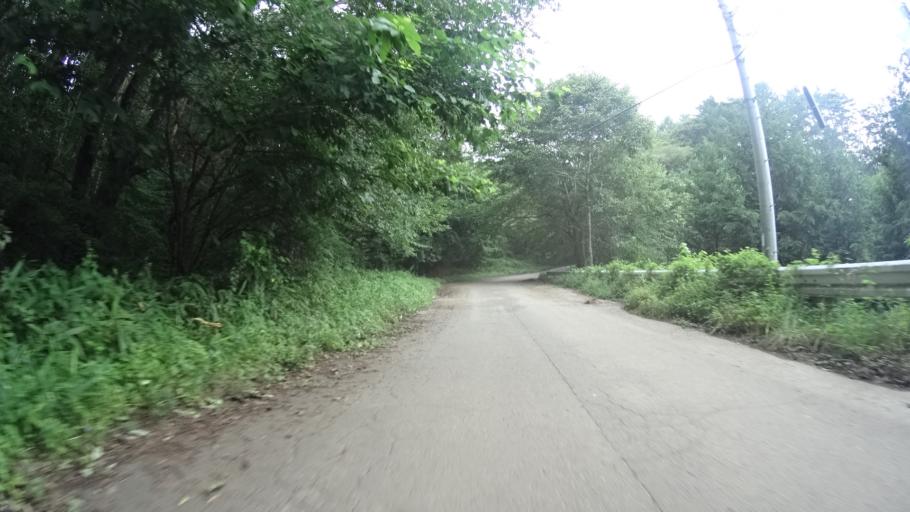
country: JP
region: Yamanashi
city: Nirasaki
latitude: 35.8965
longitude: 138.4189
